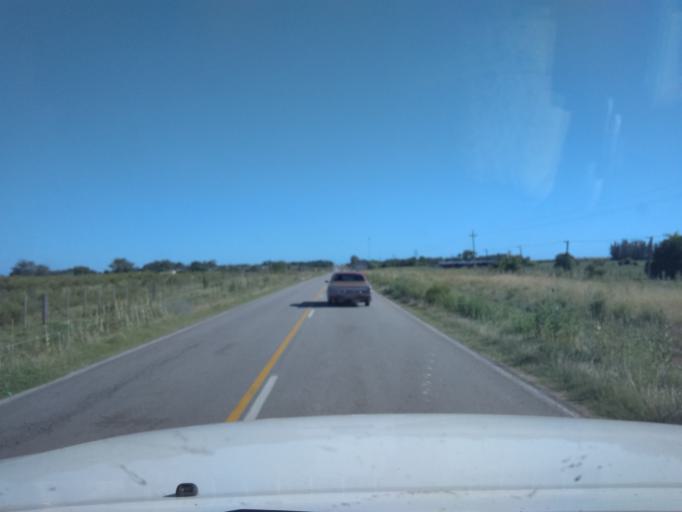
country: UY
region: Canelones
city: San Ramon
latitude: -34.3187
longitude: -55.9595
